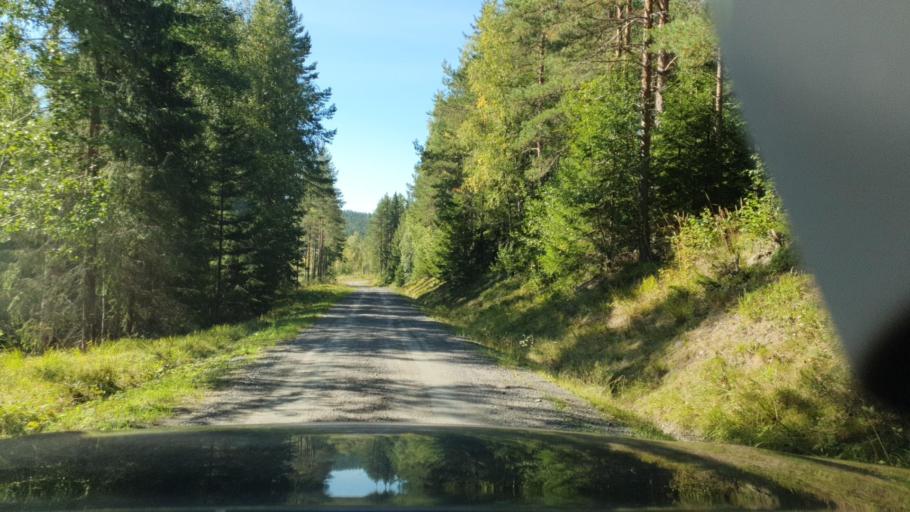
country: SE
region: Vaermland
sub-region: Filipstads Kommun
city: Lesjofors
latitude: 59.9311
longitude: 14.3010
